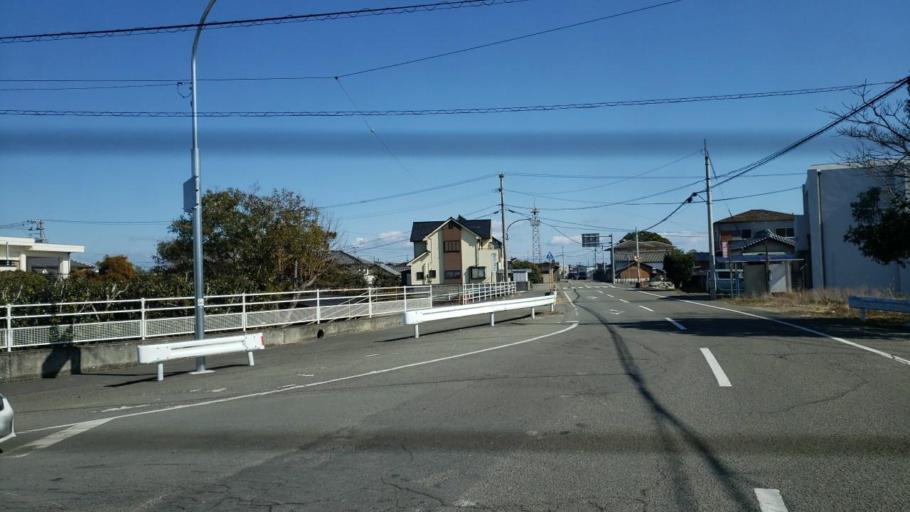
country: JP
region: Tokushima
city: Tokushima-shi
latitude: 34.1347
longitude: 134.5321
